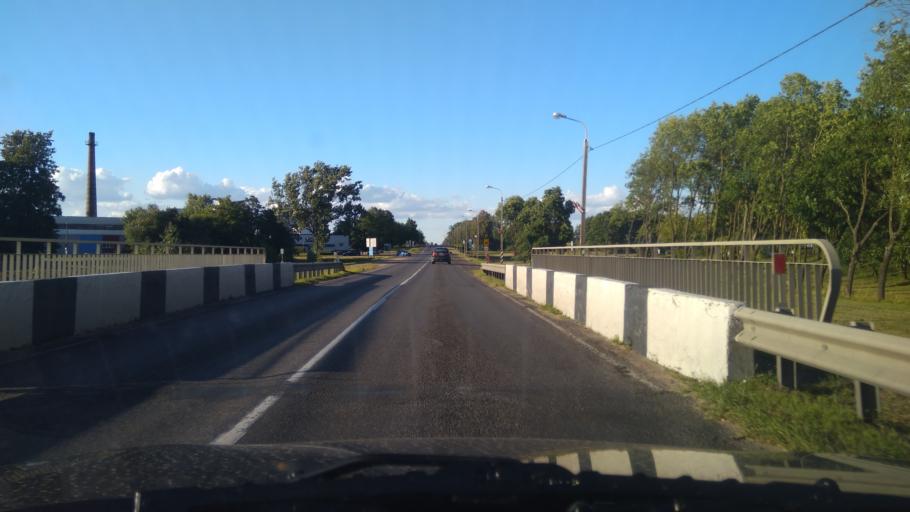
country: BY
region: Brest
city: Pruzhany
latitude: 52.5601
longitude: 24.4794
